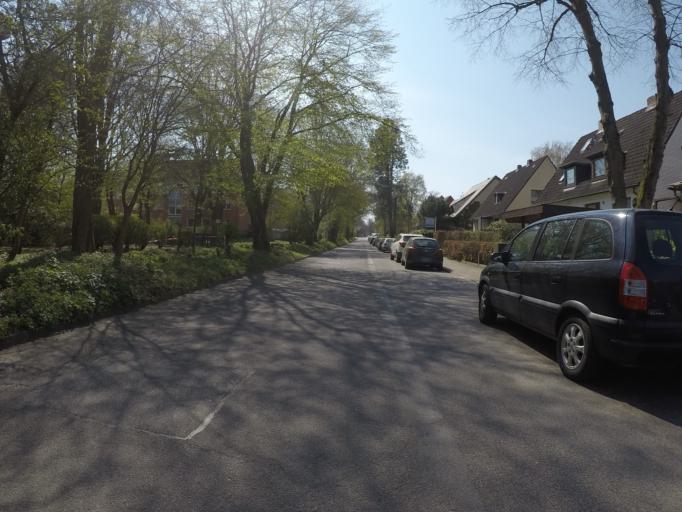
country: DE
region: Schleswig-Holstein
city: Halstenbek
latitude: 53.5843
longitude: 9.8173
